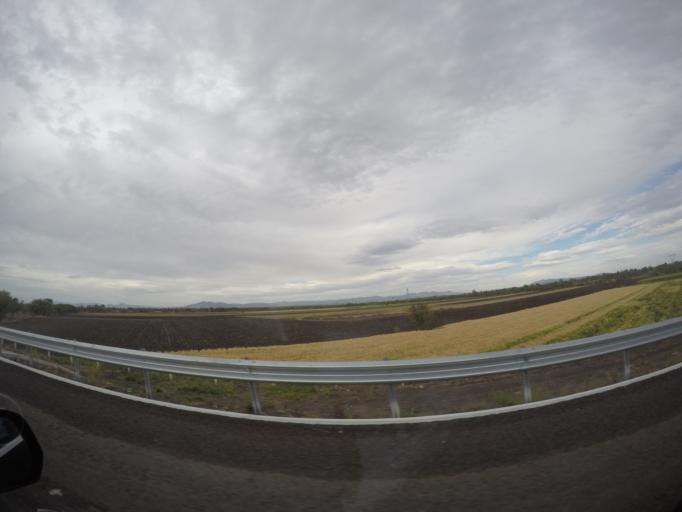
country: MX
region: Guanajuato
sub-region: Irapuato
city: Serrano
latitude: 20.8113
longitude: -101.4374
